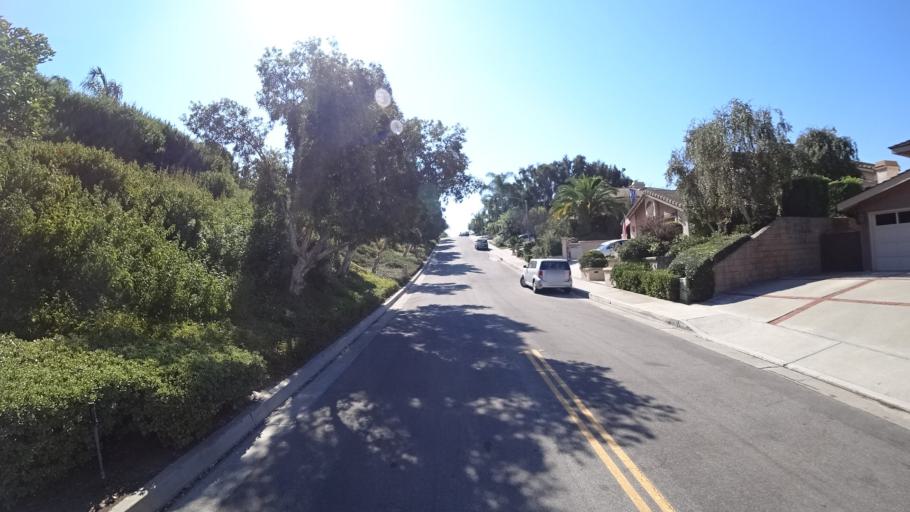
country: US
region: California
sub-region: Orange County
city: San Clemente
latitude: 33.4648
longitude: -117.6355
